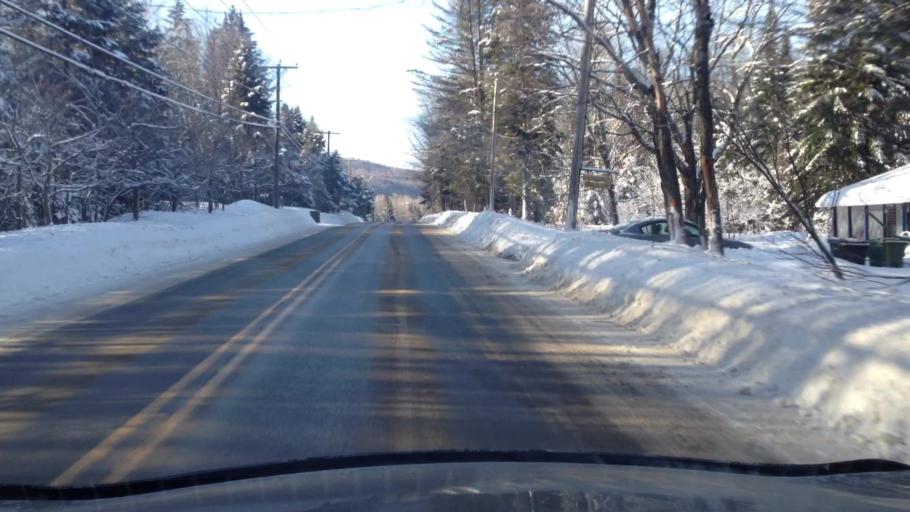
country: CA
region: Quebec
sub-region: Laurentides
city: Sainte-Agathe-des-Monts
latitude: 45.9297
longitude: -74.4110
